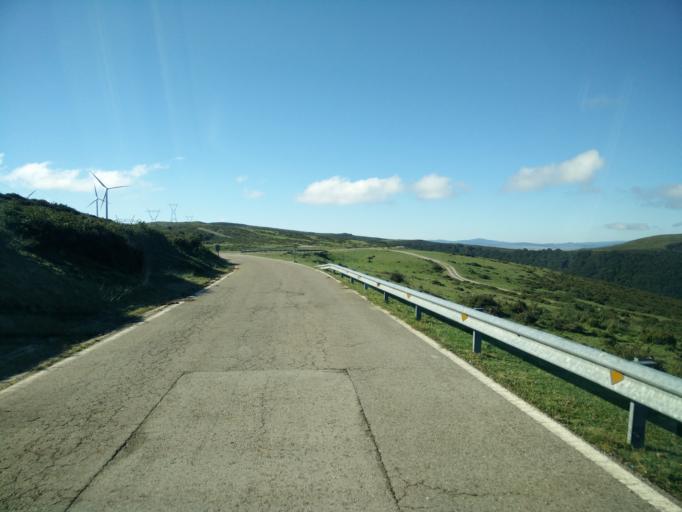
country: ES
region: Cantabria
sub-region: Provincia de Cantabria
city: San Pedro del Romeral
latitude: 43.0521
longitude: -3.8487
